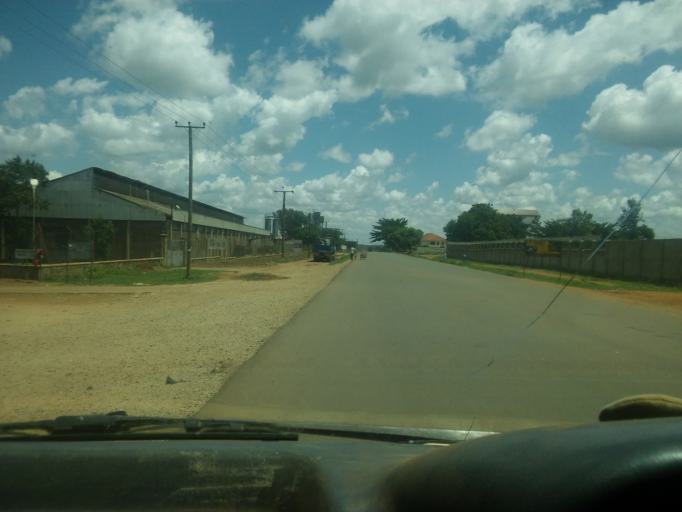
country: UG
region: Eastern Region
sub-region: Mbale District
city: Mbale
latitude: 1.0792
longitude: 34.1519
